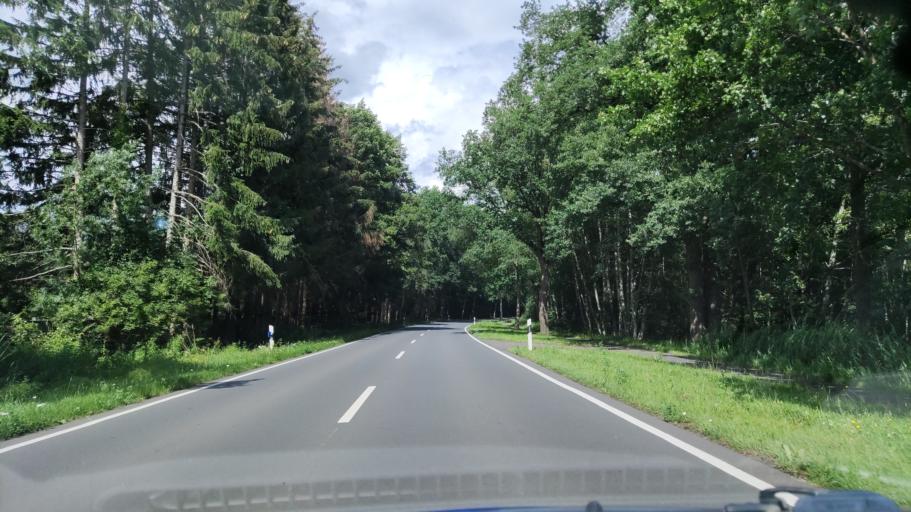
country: DE
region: Lower Saxony
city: Bad Fallingbostel
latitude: 52.9128
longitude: 9.7720
